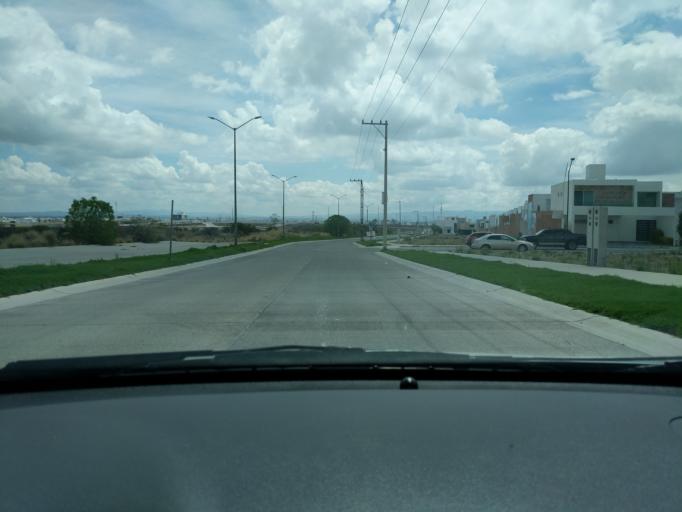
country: MX
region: San Luis Potosi
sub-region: Mexquitic de Carmona
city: Guadalupe Victoria
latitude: 22.1615
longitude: -101.0520
